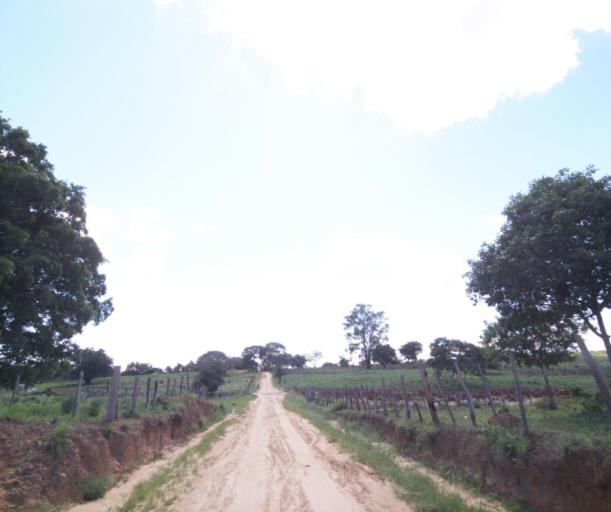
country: BR
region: Bahia
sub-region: Carinhanha
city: Carinhanha
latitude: -14.2346
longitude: -44.3137
